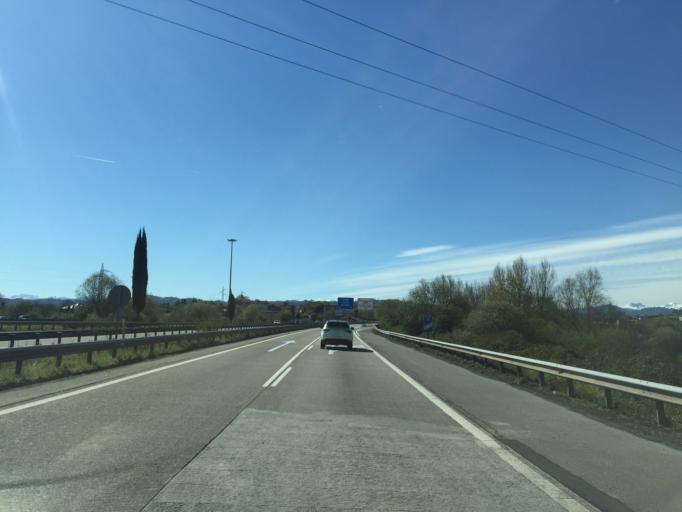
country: ES
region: Asturias
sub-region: Province of Asturias
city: Lugones
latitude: 43.4113
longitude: -5.7993
